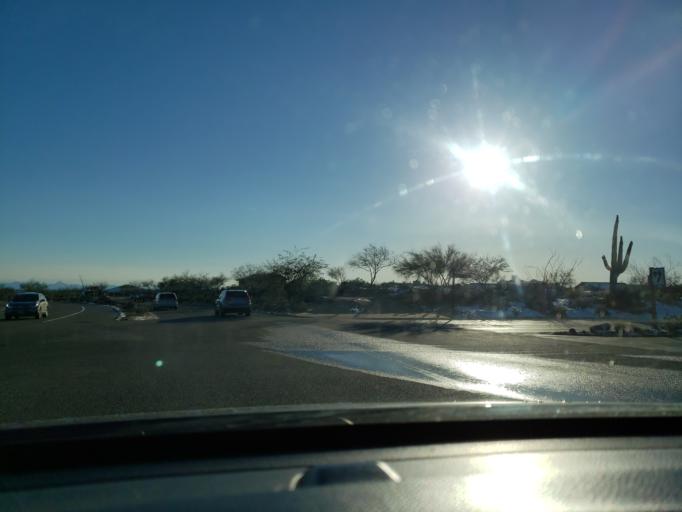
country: US
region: Arizona
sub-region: Maricopa County
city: Carefree
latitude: 33.8368
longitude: -111.8520
